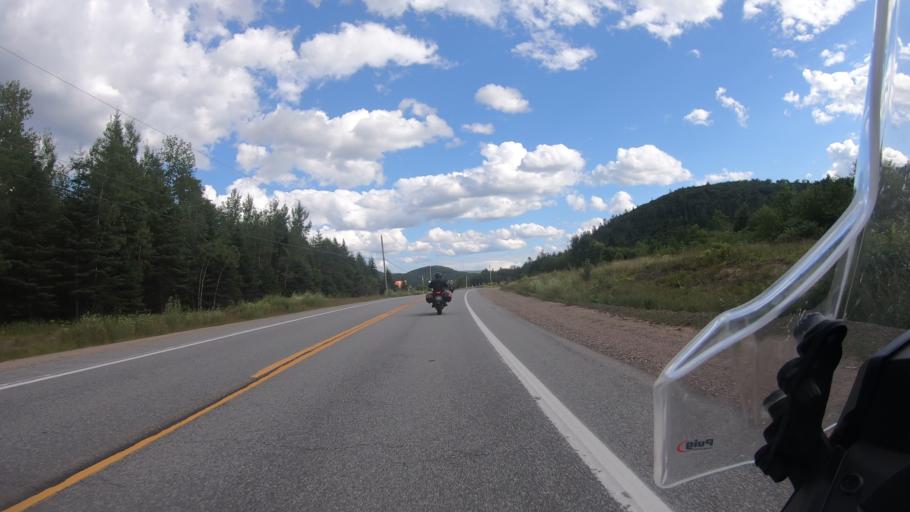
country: CA
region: Quebec
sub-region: Mauricie
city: Saint-Tite
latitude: 46.9878
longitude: -72.9116
